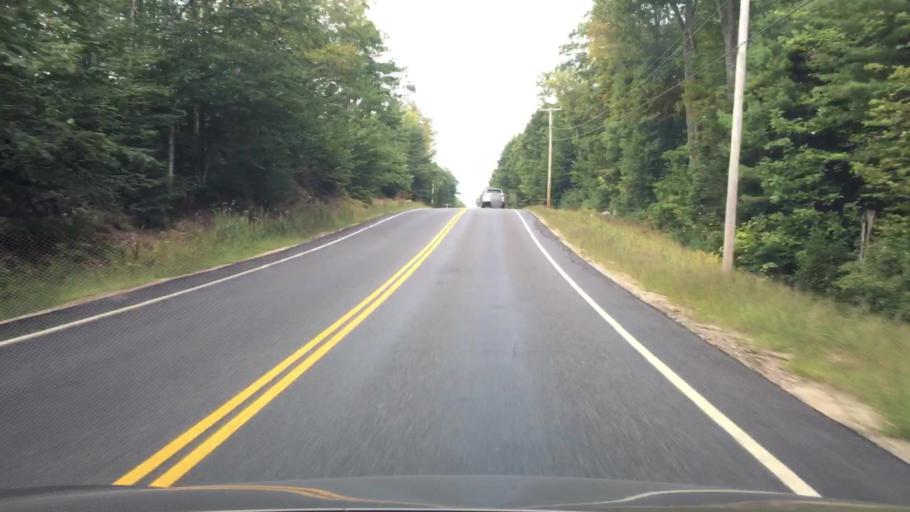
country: US
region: Maine
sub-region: Oxford County
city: Hartford
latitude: 44.3656
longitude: -70.3218
